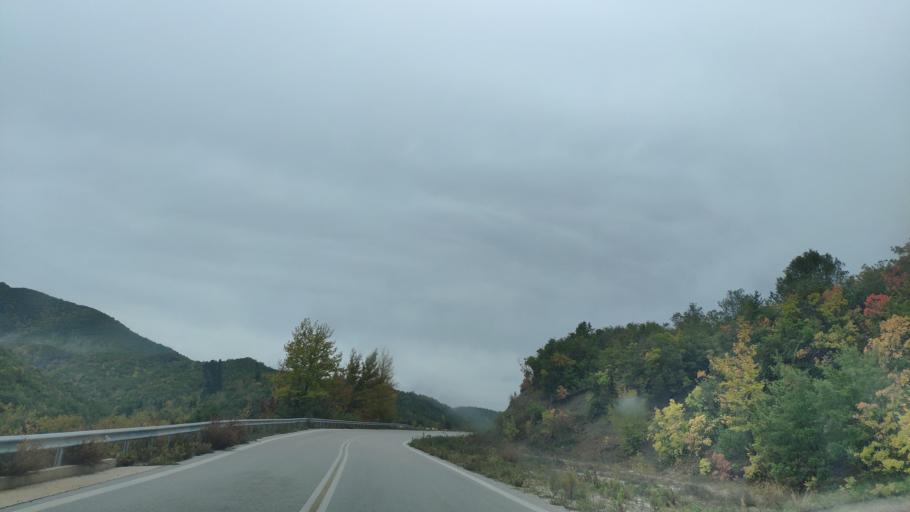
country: GR
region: Epirus
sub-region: Nomos Thesprotias
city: Paramythia
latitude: 39.4884
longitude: 20.6709
